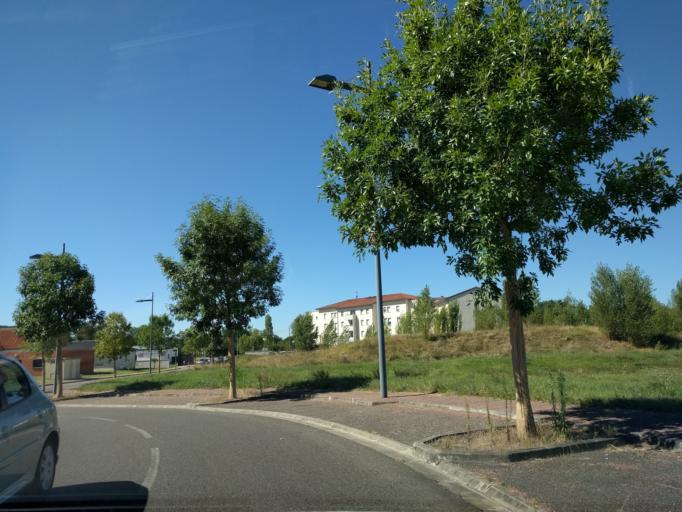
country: FR
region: Midi-Pyrenees
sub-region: Departement du Tarn-et-Garonne
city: Montauban
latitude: 44.0390
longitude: 1.3520
